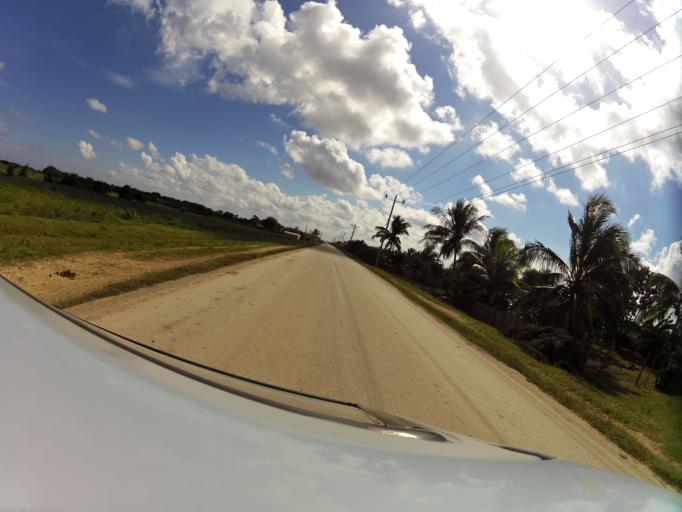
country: CU
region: Las Tunas
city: Jesus Menendez
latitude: 21.2230
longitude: -76.4224
